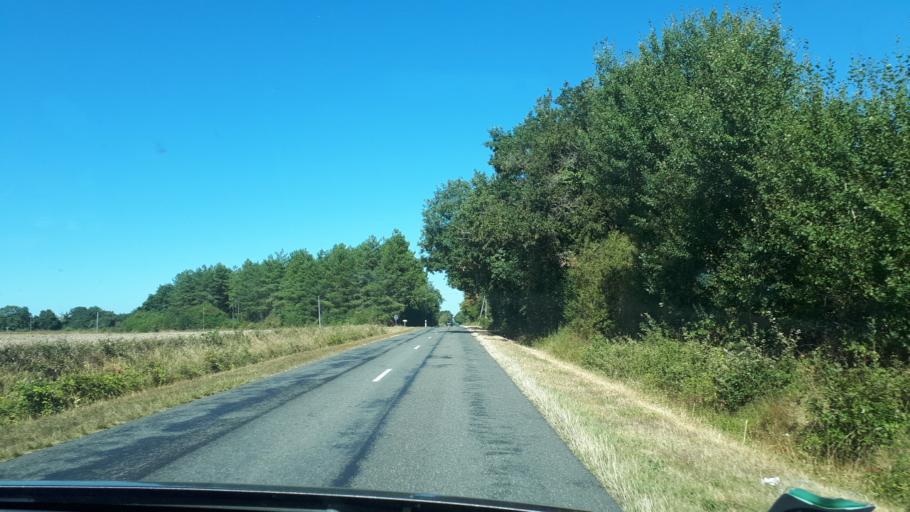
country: FR
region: Centre
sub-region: Departement du Loiret
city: Coullons
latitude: 47.6324
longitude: 2.4639
